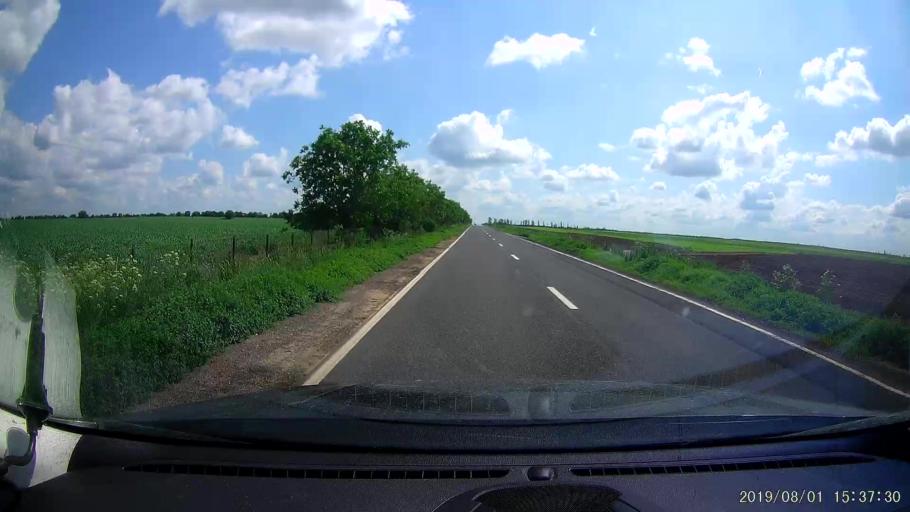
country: RO
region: Braila
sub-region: Comuna Insuratei
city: Insuratei
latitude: 44.9016
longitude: 27.5883
